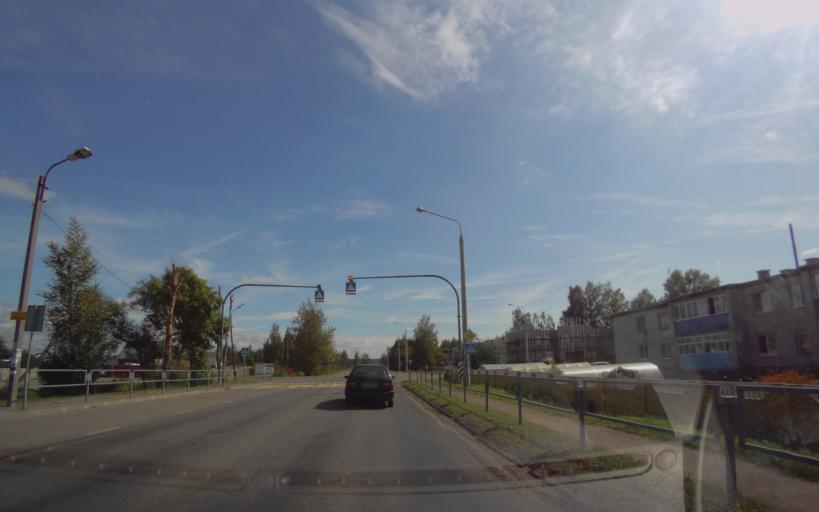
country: BY
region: Minsk
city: Horad Barysaw
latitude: 54.1948
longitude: 28.5499
